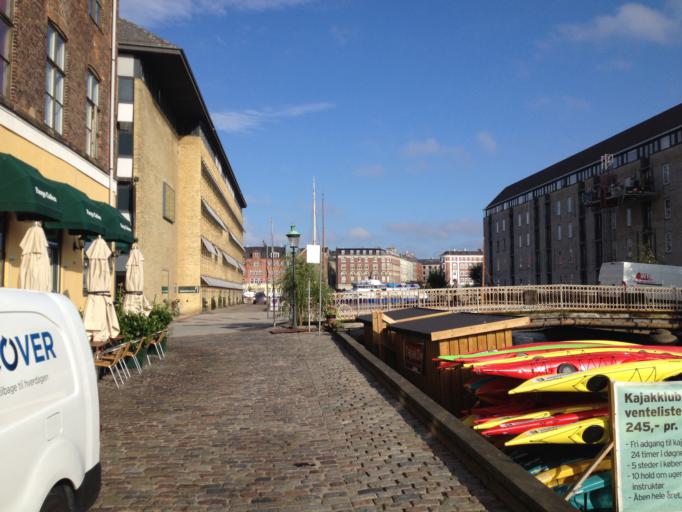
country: DK
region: Capital Region
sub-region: Kobenhavn
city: Christianshavn
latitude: 55.6754
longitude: 12.5928
